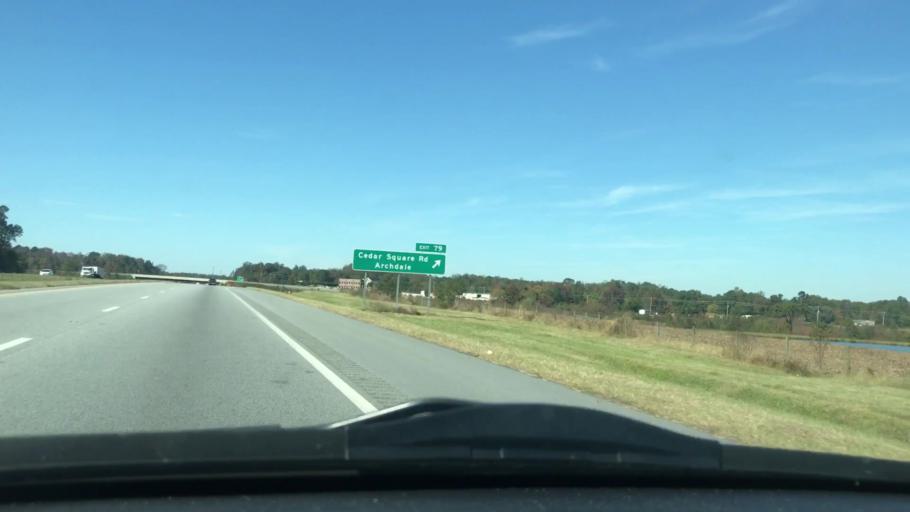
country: US
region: North Carolina
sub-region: Randolph County
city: Archdale
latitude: 35.8697
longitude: -79.8967
